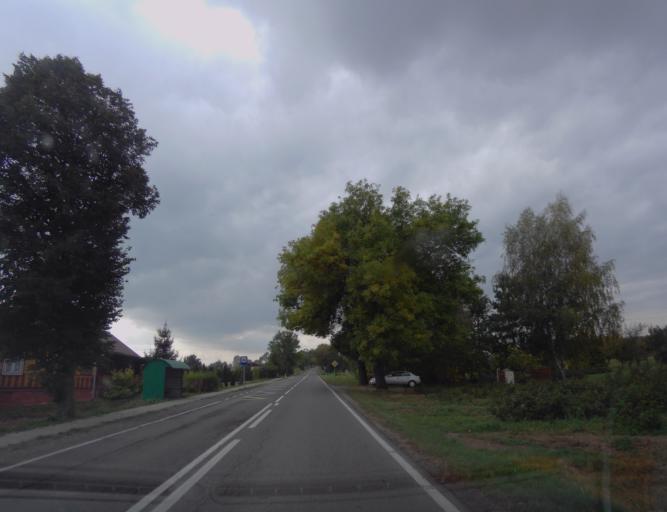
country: PL
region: Lublin Voivodeship
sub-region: Powiat krasnostawski
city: Zolkiewka
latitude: 50.9275
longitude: 22.9005
